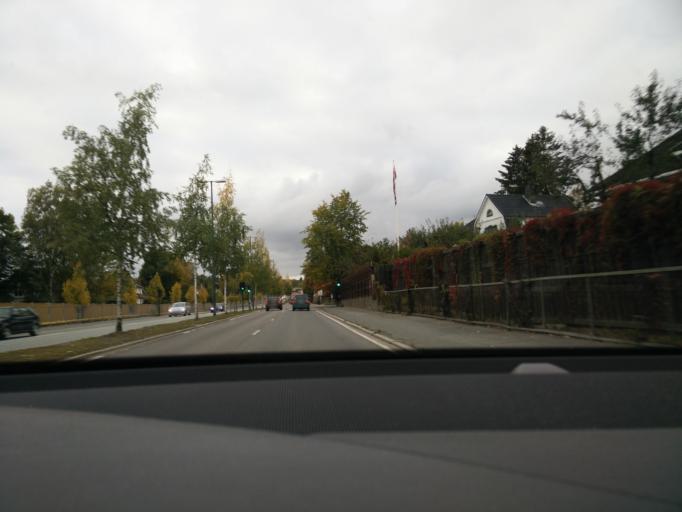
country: NO
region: Oslo
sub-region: Oslo
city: Sjolyststranda
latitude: 59.9356
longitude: 10.6922
